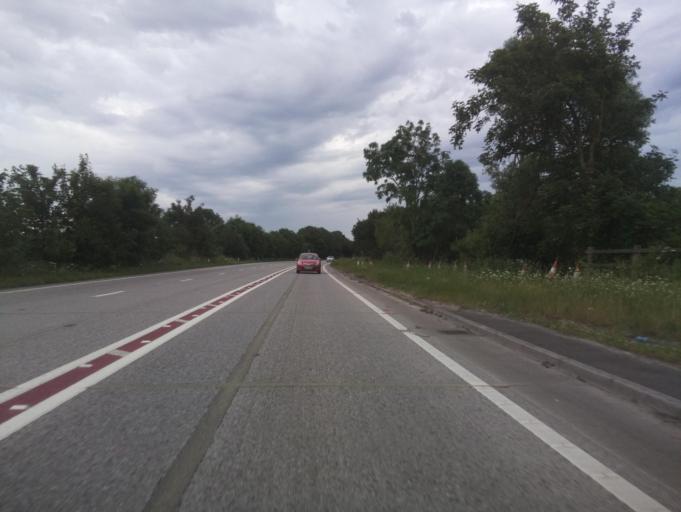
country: GB
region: England
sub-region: Somerset
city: Ilminster
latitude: 50.9450
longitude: -2.9202
